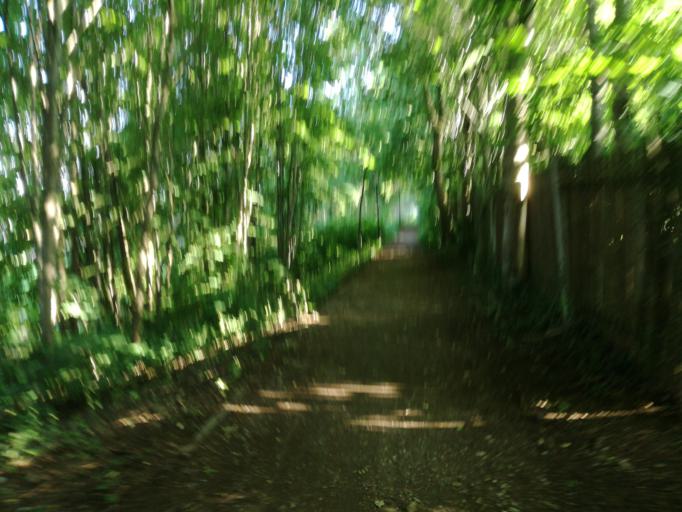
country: DE
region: Bavaria
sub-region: Upper Bavaria
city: Grafelfing
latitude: 48.1132
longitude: 11.4227
